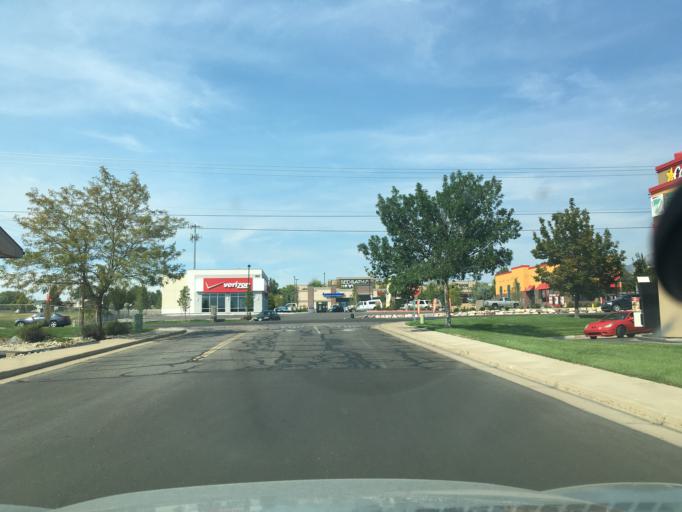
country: US
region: Utah
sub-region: Davis County
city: Hill Air Force Bace
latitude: 41.0887
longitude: -111.9828
